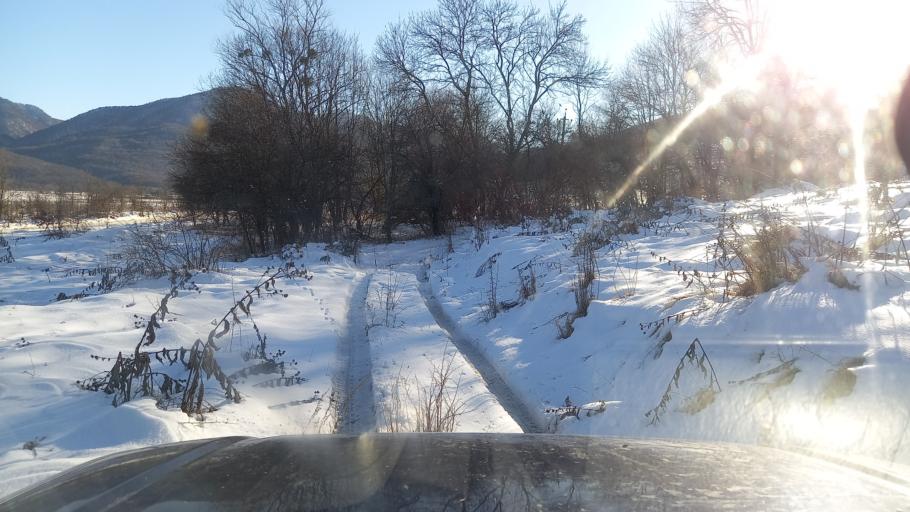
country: RU
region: Adygeya
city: Kamennomostskiy
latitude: 44.2003
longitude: 40.1499
